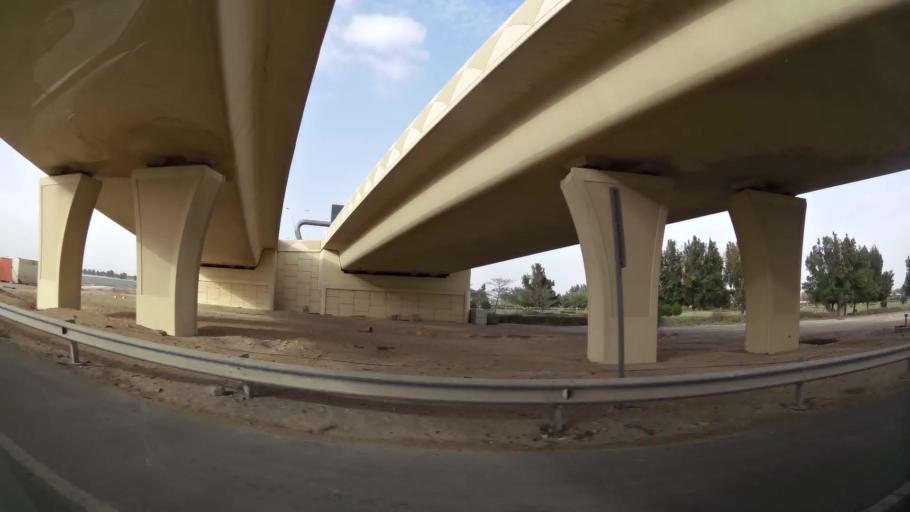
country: AE
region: Abu Dhabi
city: Abu Dhabi
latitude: 24.4928
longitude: 54.6199
